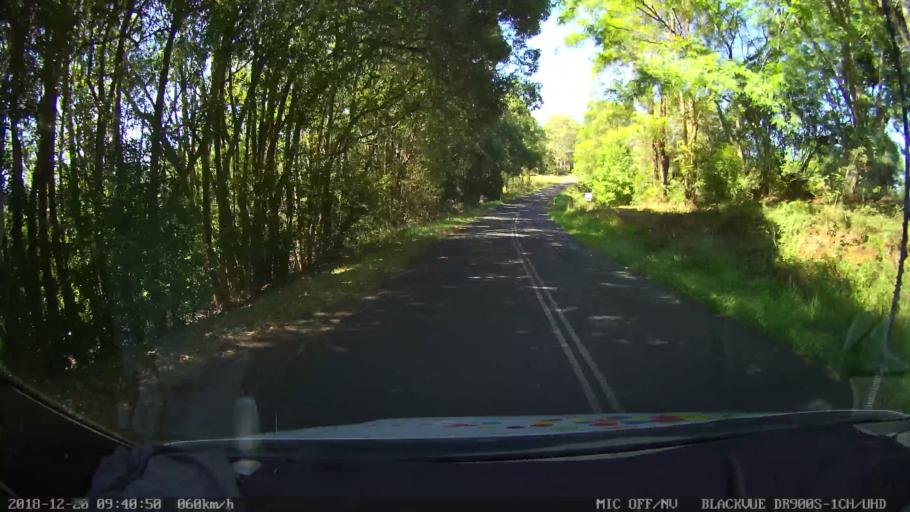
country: AU
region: New South Wales
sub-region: Lismore Municipality
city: Lismore
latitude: -28.7042
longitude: 153.3030
